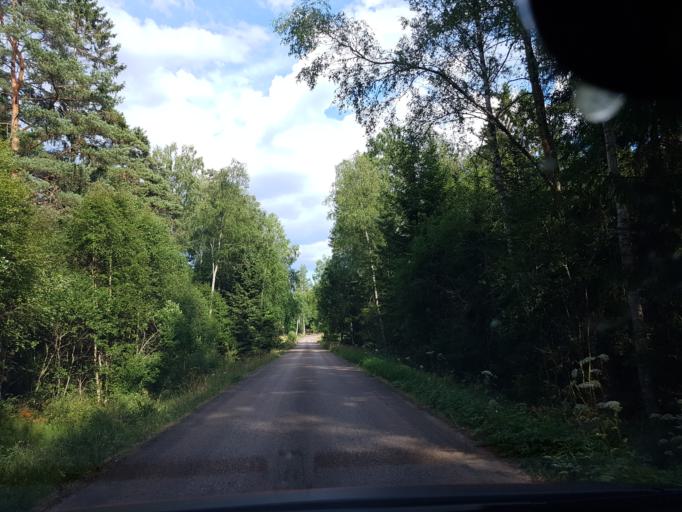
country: SE
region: Joenkoeping
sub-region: Gislaveds Kommun
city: Reftele
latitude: 57.2091
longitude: 13.5877
